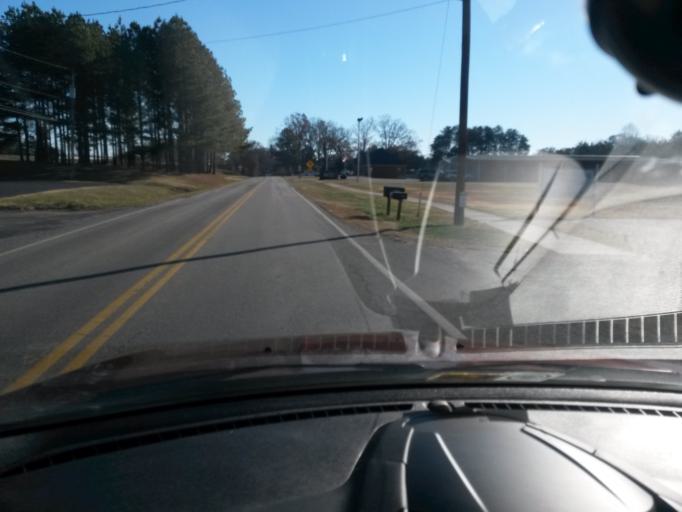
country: US
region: Virginia
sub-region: Charlotte County
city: Charlotte Court House
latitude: 37.0566
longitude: -78.6330
